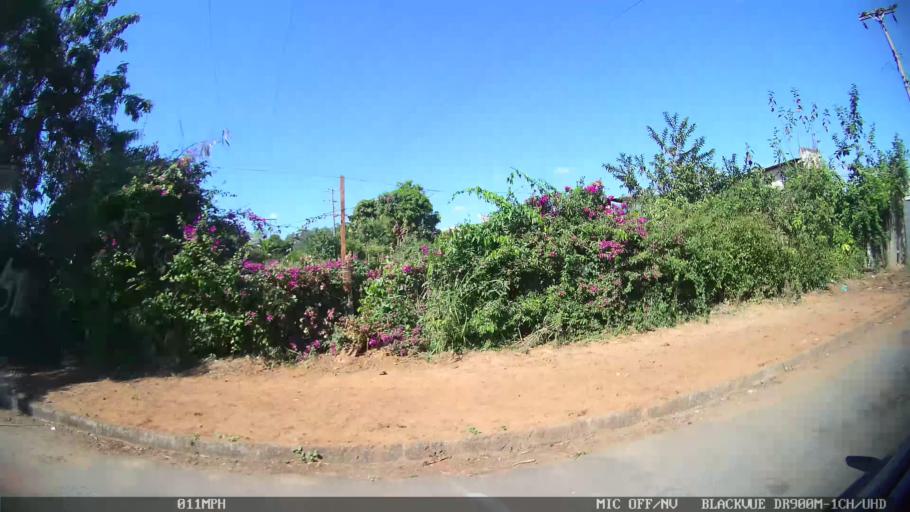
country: BR
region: Sao Paulo
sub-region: Santa Barbara D'Oeste
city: Santa Barbara d'Oeste
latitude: -22.7422
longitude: -47.4104
